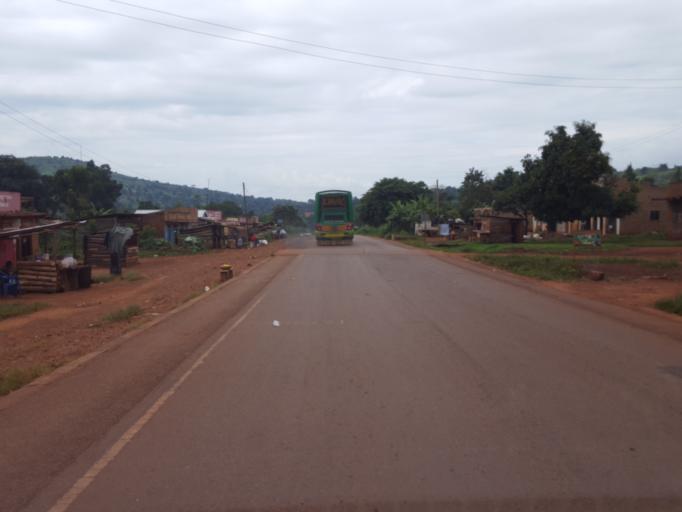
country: UG
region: Central Region
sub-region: Mityana District
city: Mityana
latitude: 0.6618
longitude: 32.0910
